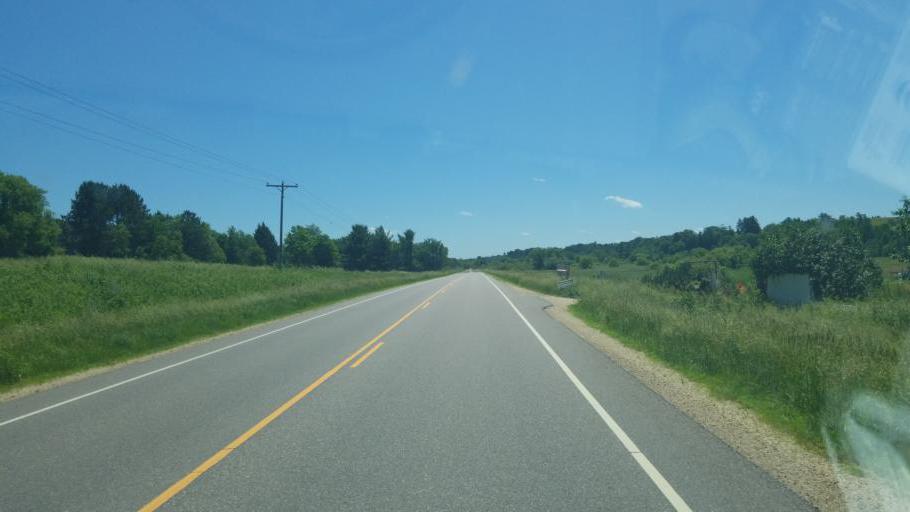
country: US
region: Wisconsin
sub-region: Juneau County
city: Elroy
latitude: 43.7812
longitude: -90.2761
